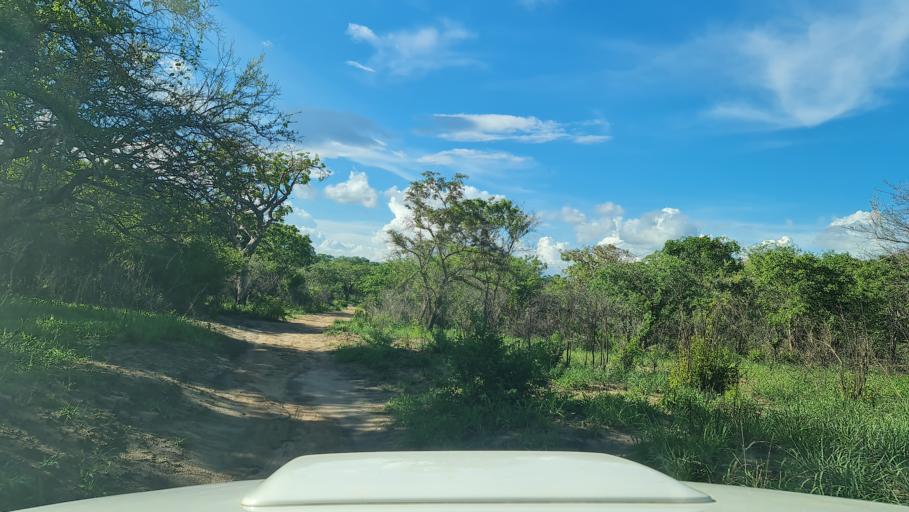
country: MZ
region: Nampula
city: Ilha de Mocambique
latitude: -15.2572
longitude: 40.1837
